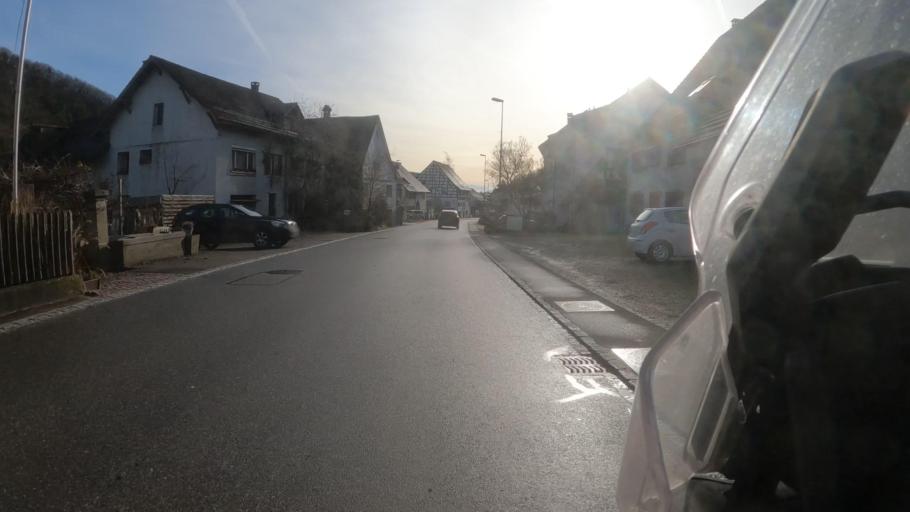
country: CH
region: Schaffhausen
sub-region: Bezirk Reiat
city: Stetten
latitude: 47.7610
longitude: 8.6092
